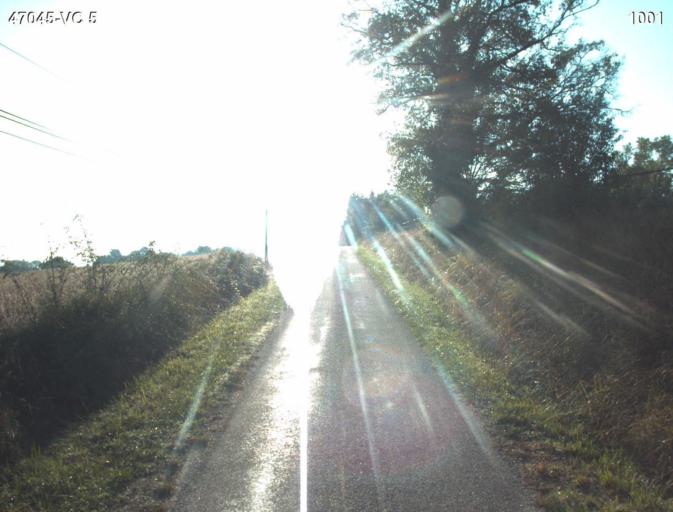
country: FR
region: Aquitaine
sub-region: Departement du Lot-et-Garonne
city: Nerac
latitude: 44.1387
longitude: 0.4052
